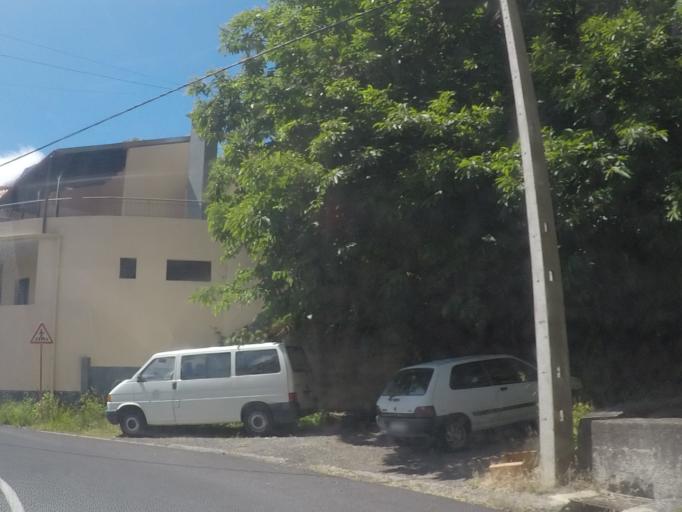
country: PT
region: Madeira
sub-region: Camara de Lobos
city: Curral das Freiras
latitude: 32.7195
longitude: -16.9641
